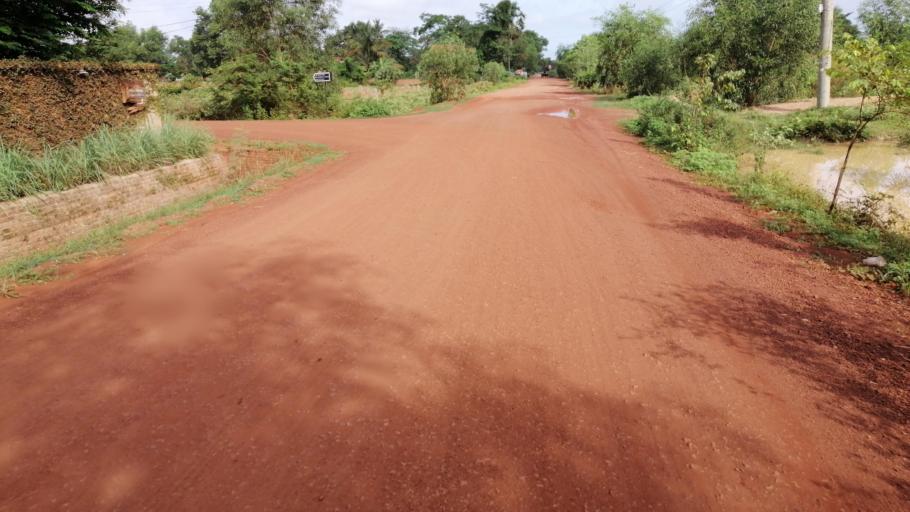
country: KH
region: Siem Reap
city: Siem Reap
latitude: 13.3589
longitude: 103.8278
